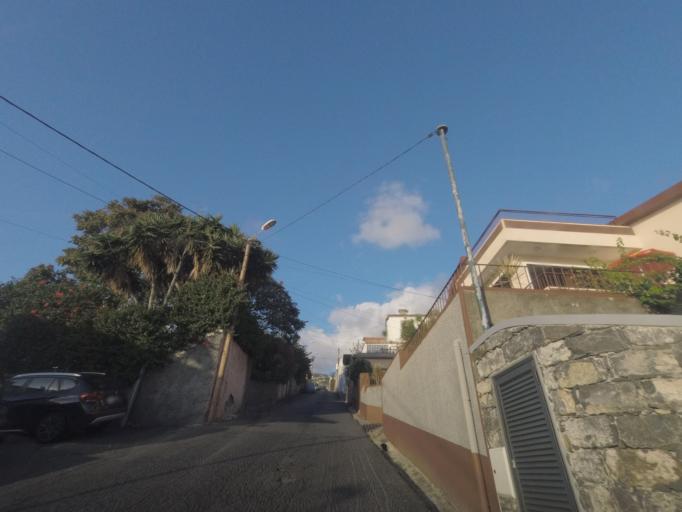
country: PT
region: Madeira
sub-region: Funchal
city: Funchal
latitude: 32.6471
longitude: -16.8855
